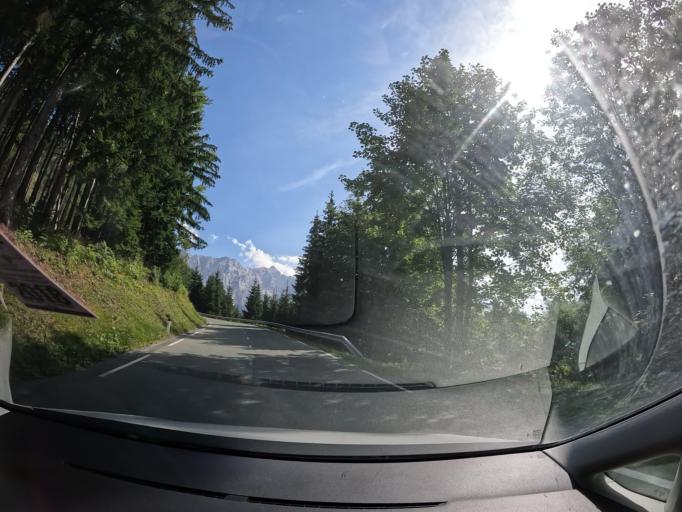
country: AT
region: Carinthia
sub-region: Politischer Bezirk Sankt Veit an der Glan
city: Liebenfels
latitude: 46.7086
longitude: 14.2748
